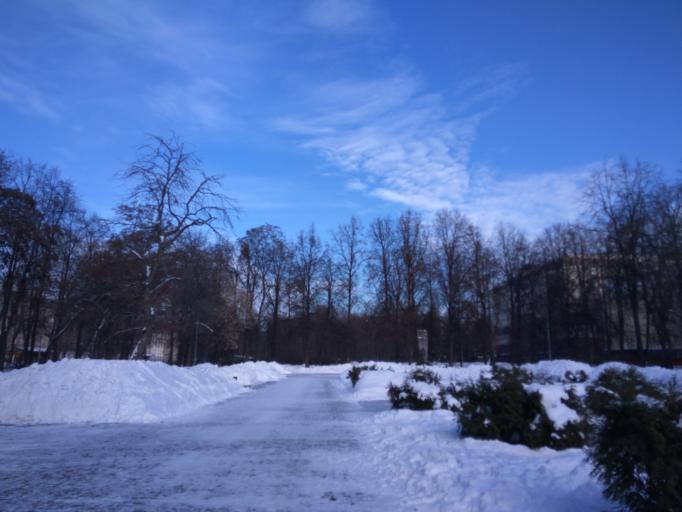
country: RU
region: Moscow
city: Lefortovo
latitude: 55.7595
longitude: 37.6957
